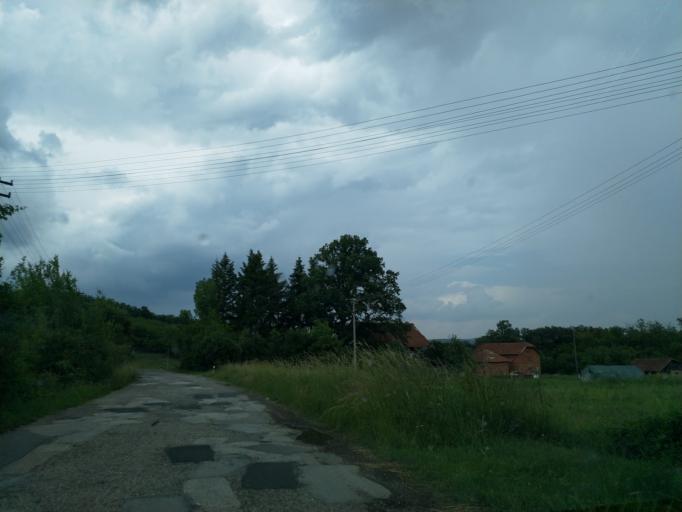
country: RS
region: Central Serbia
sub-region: Borski Okrug
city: Bor
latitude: 43.9891
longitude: 21.9747
